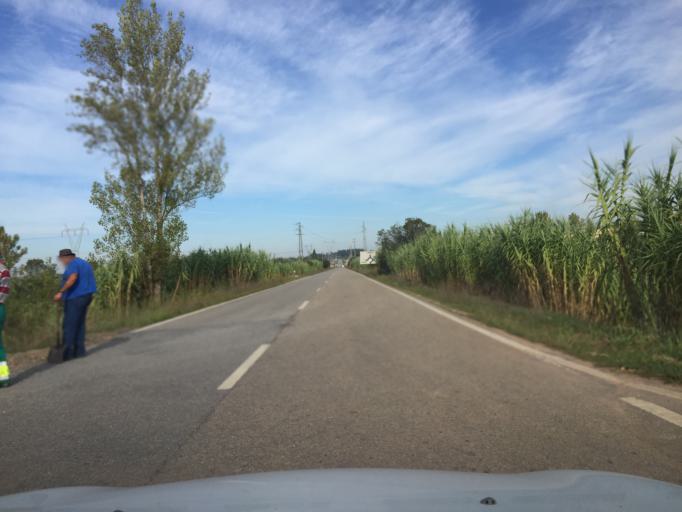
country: PT
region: Aveiro
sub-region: Anadia
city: Anadia
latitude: 40.4374
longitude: -8.4196
